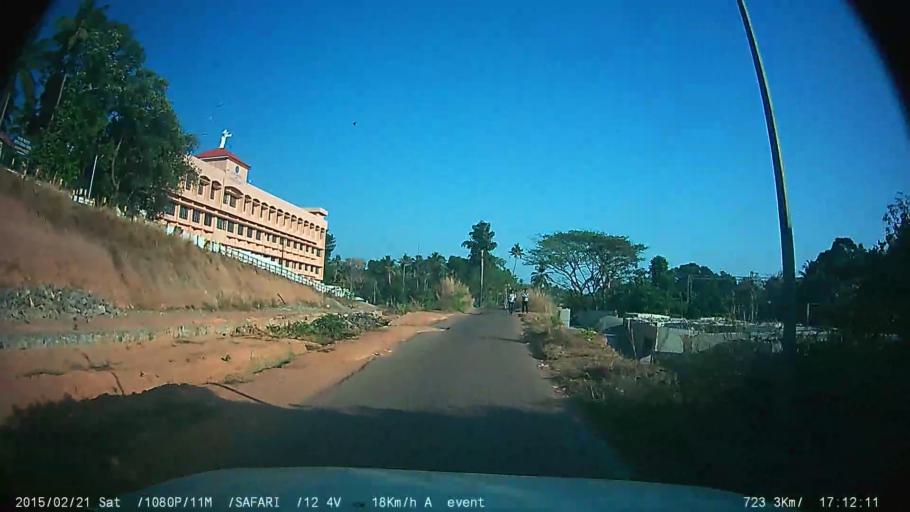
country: IN
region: Kerala
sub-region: Kottayam
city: Changanacheri
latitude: 9.4490
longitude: 76.5494
